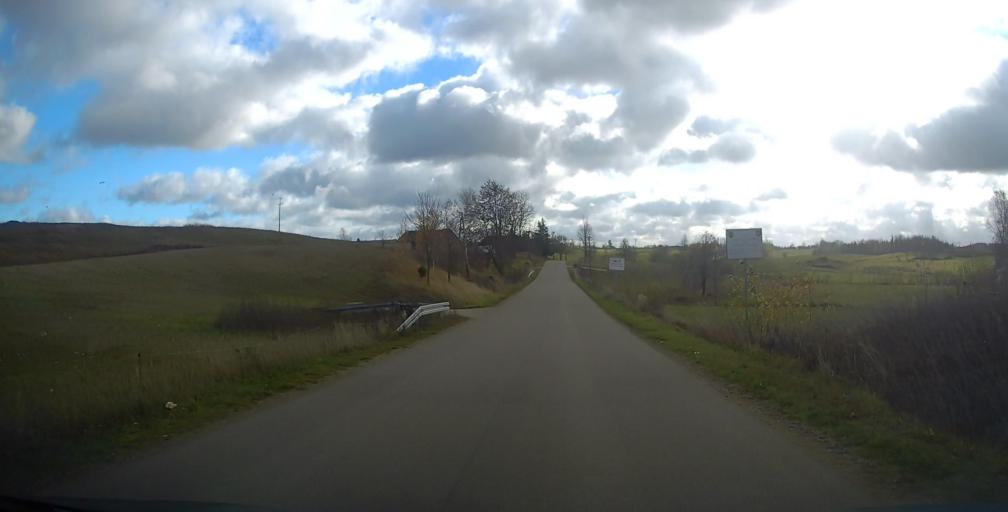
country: PL
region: Podlasie
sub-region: Suwalki
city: Suwalki
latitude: 54.3282
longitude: 22.8612
